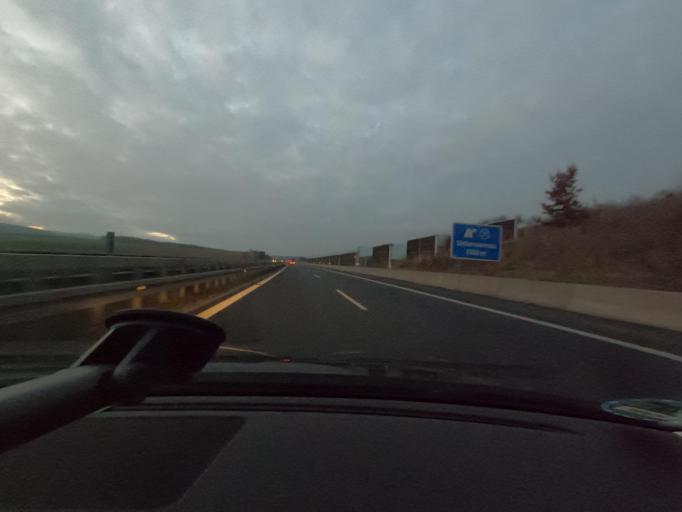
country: DE
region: Bavaria
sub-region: Upper Franconia
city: Lichtenfels
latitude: 50.1524
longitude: 11.0261
